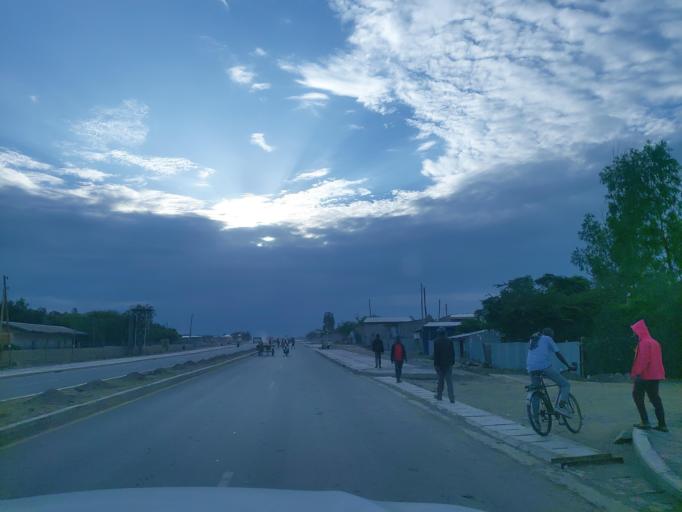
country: ET
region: Oromiya
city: Ziway
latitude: 8.1457
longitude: 38.8074
